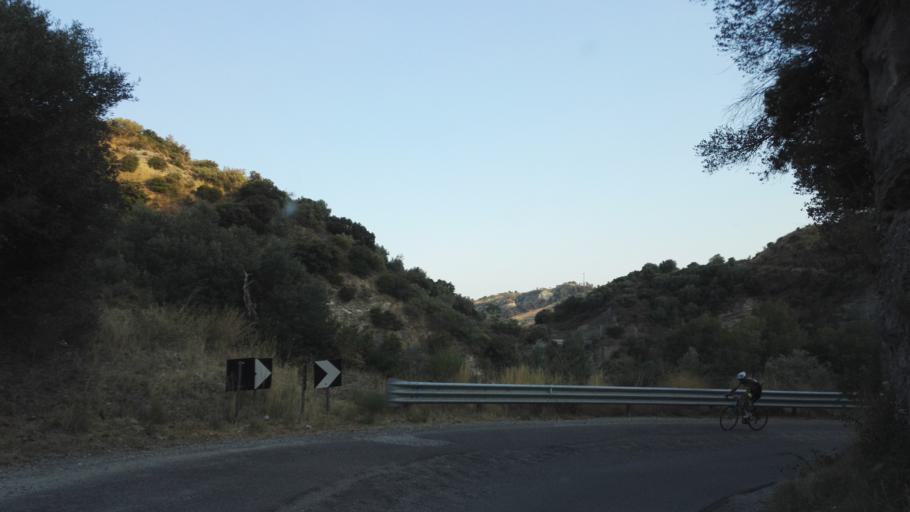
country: IT
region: Calabria
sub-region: Provincia di Reggio Calabria
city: Caulonia
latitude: 38.3999
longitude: 16.4138
